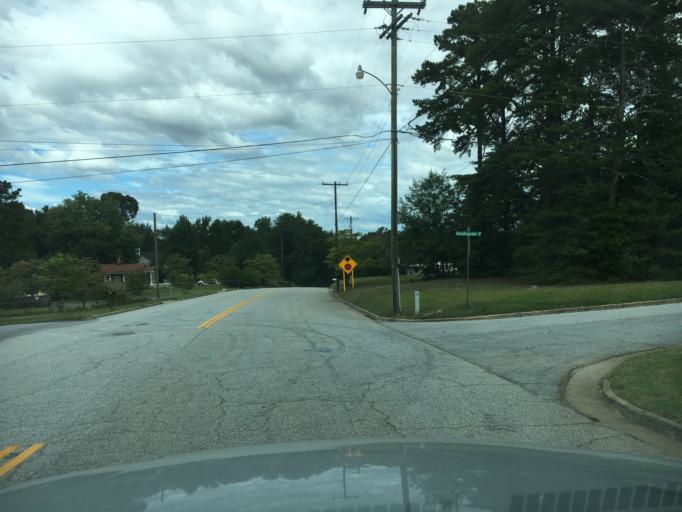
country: US
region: South Carolina
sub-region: Greenville County
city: Greer
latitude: 34.9464
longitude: -82.2304
